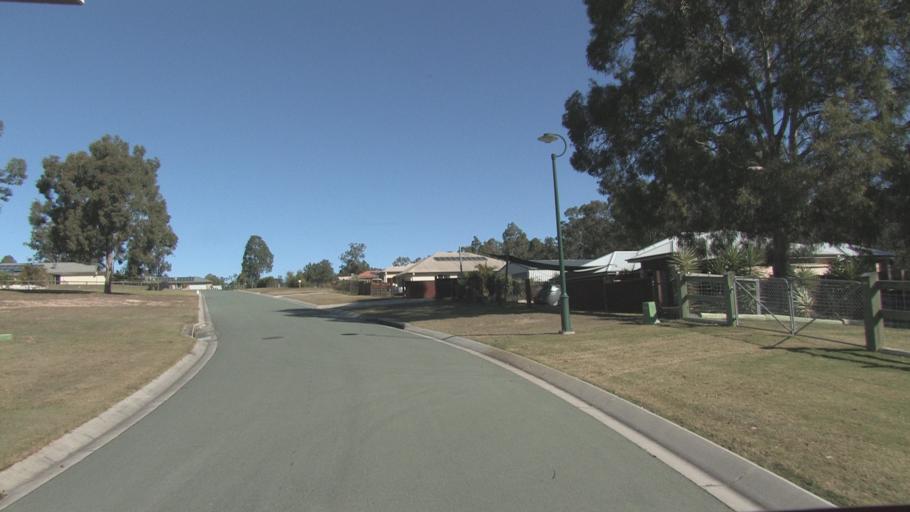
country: AU
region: Queensland
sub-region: Ipswich
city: Springfield Lakes
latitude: -27.7289
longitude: 152.9354
